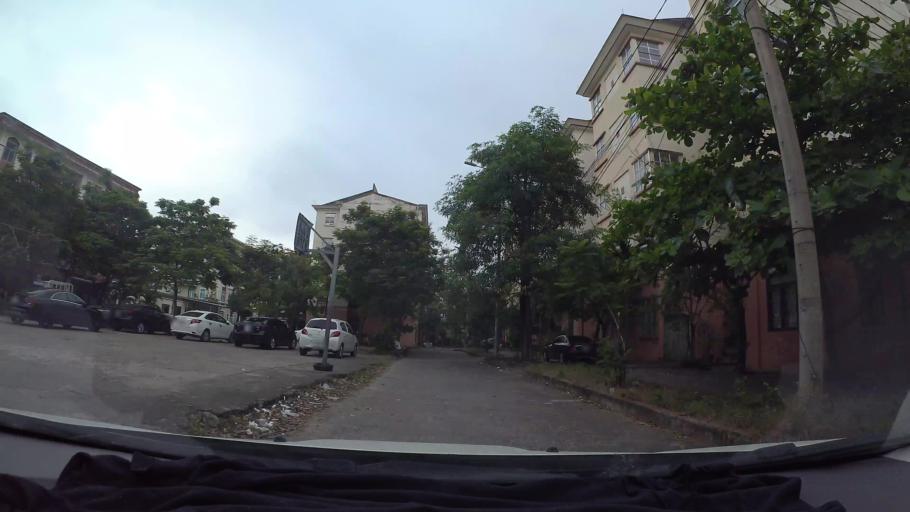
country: VN
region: Da Nang
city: Thanh Khe
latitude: 16.0704
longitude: 108.1927
